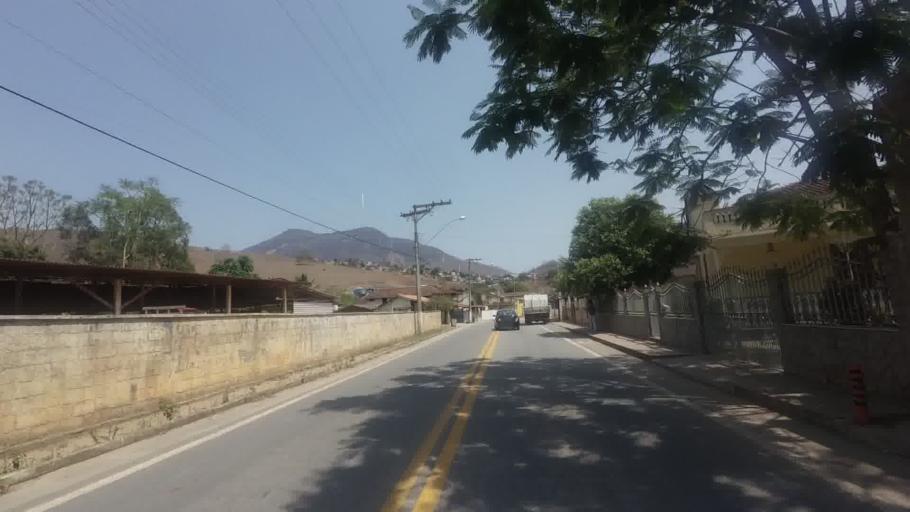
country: BR
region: Espirito Santo
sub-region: Mimoso Do Sul
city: Mimoso do Sul
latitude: -20.9446
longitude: -41.3358
